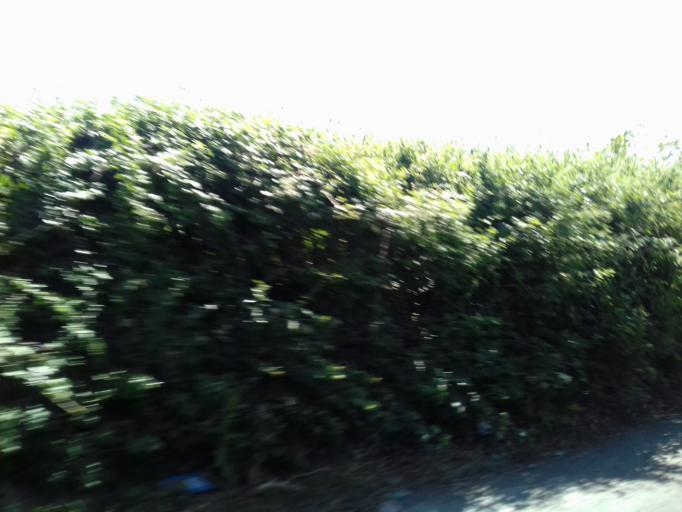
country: IE
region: Leinster
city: Ballymun
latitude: 53.4428
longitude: -6.2935
